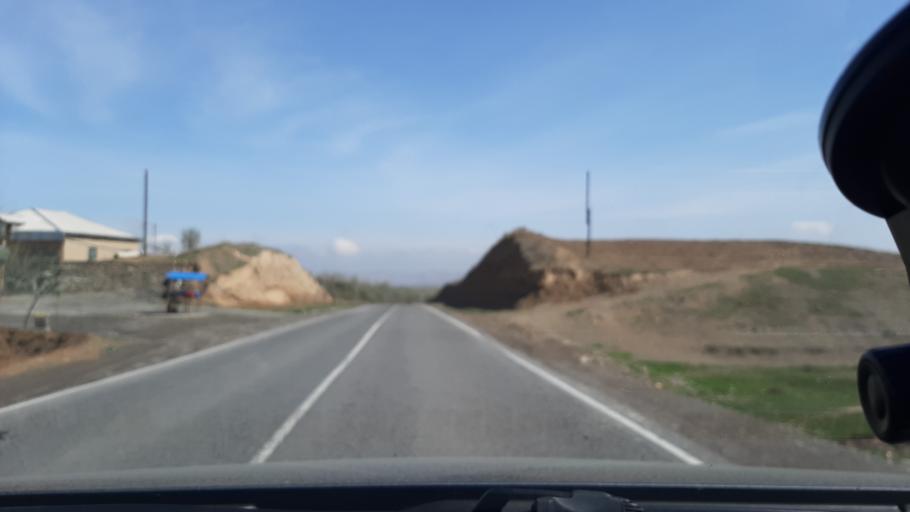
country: TJ
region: Viloyati Sughd
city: Shahriston
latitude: 39.7741
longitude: 68.8273
